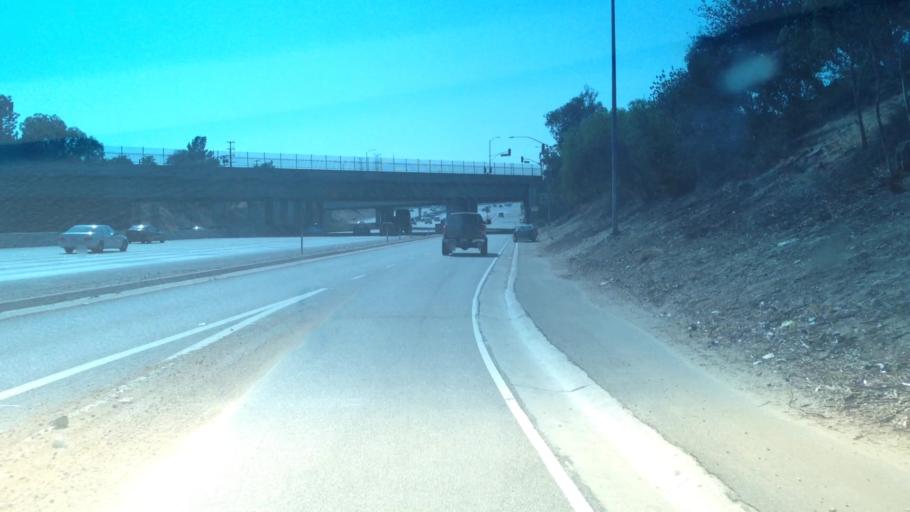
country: US
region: California
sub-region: Los Angeles County
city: San Fernando
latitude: 34.2315
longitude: -118.4017
